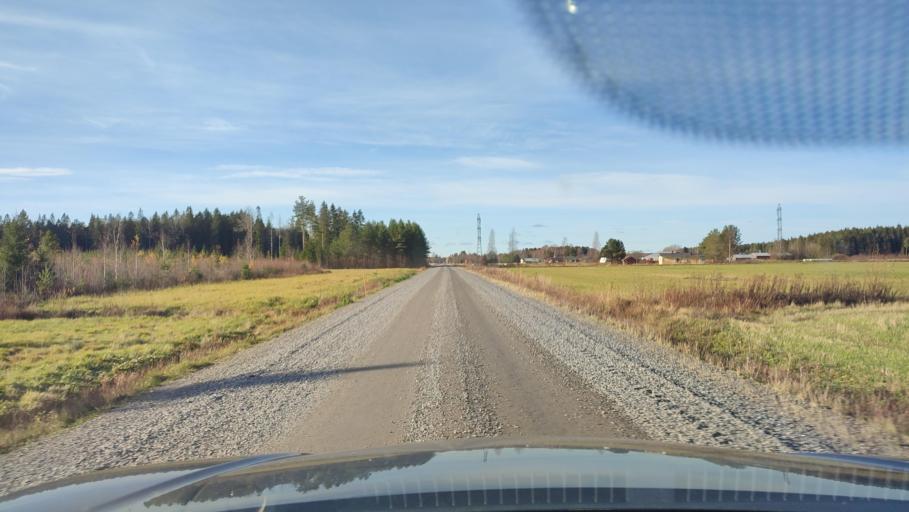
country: FI
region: Southern Ostrobothnia
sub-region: Suupohja
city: Teuva
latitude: 62.4577
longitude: 21.6523
